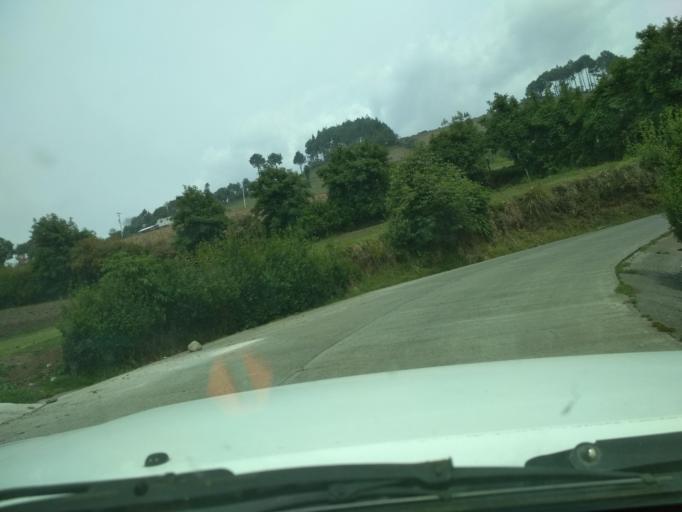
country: MX
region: Veracruz
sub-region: Mariano Escobedo
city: San Isidro el Berro
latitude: 18.9752
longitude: -97.2055
